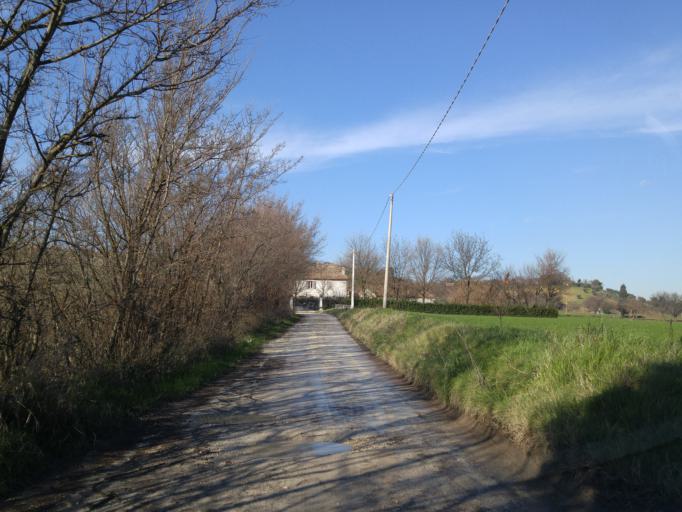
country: IT
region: The Marches
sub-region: Provincia di Pesaro e Urbino
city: Calcinelli
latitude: 43.7568
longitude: 12.9149
